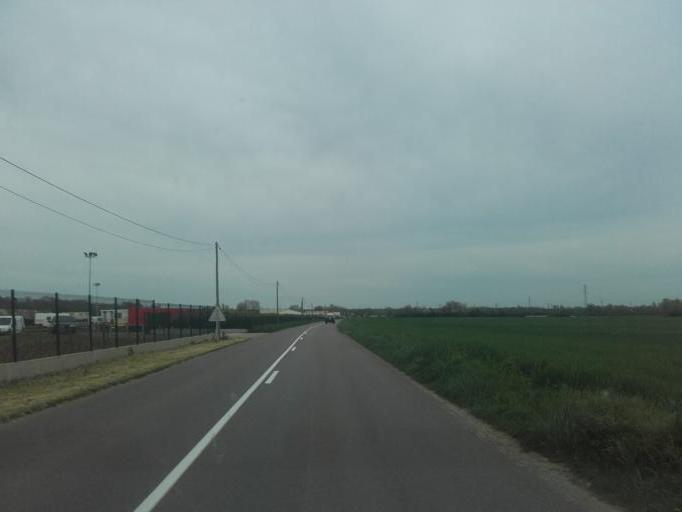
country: FR
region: Bourgogne
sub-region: Departement de la Cote-d'Or
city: Bligny-les-Beaune
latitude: 46.9671
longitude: 4.8006
